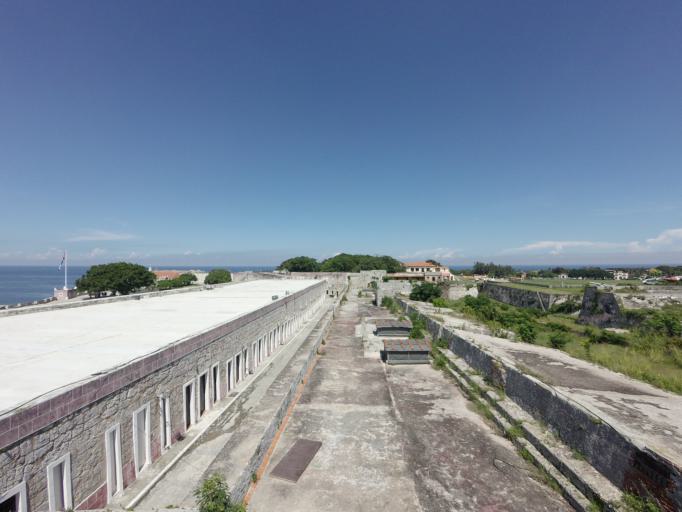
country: CU
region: La Habana
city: La Habana Vieja
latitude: 23.1456
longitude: -82.3482
